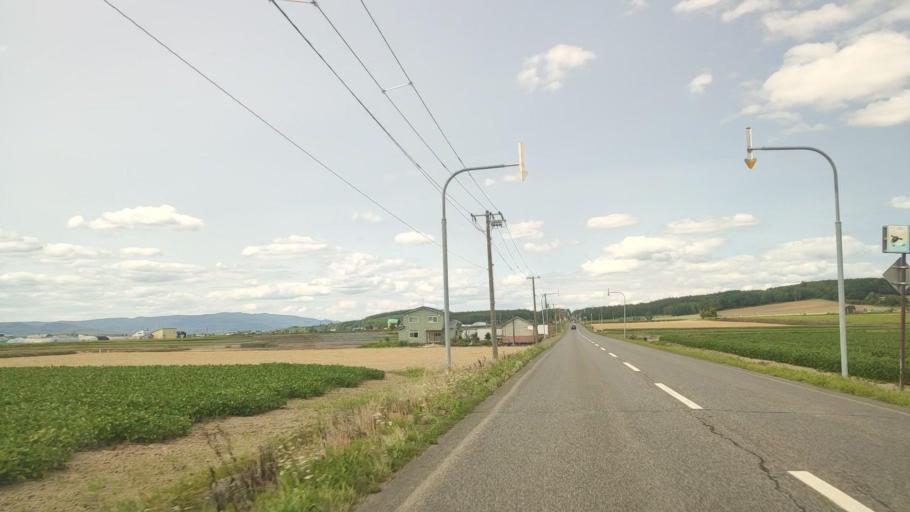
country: JP
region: Hokkaido
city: Nayoro
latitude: 44.2312
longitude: 142.4157
